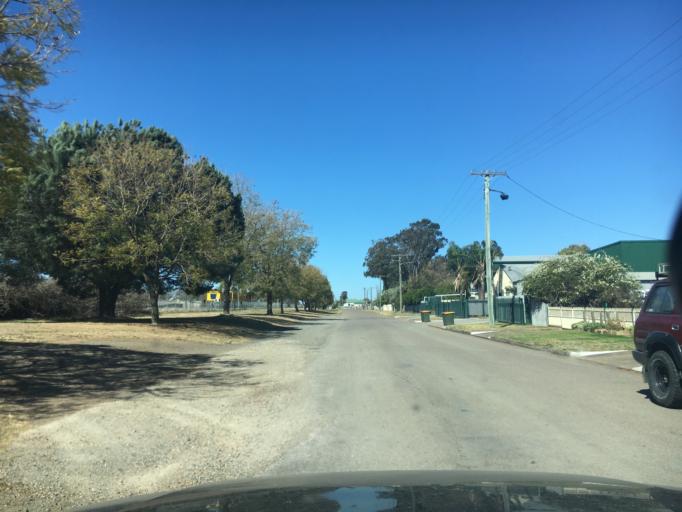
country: AU
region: New South Wales
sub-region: Singleton
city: Singleton
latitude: -32.5728
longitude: 151.1658
